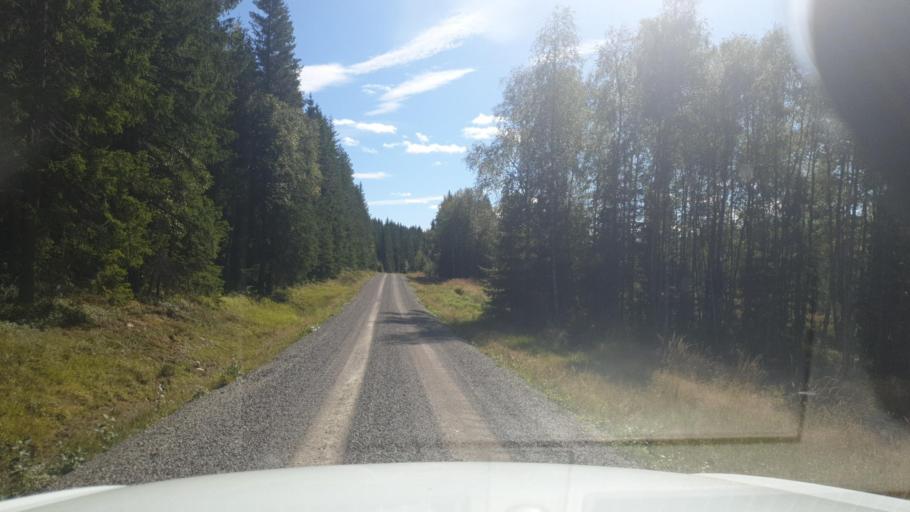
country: SE
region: Vaermland
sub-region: Eda Kommun
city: Charlottenberg
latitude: 60.0838
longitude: 12.6184
